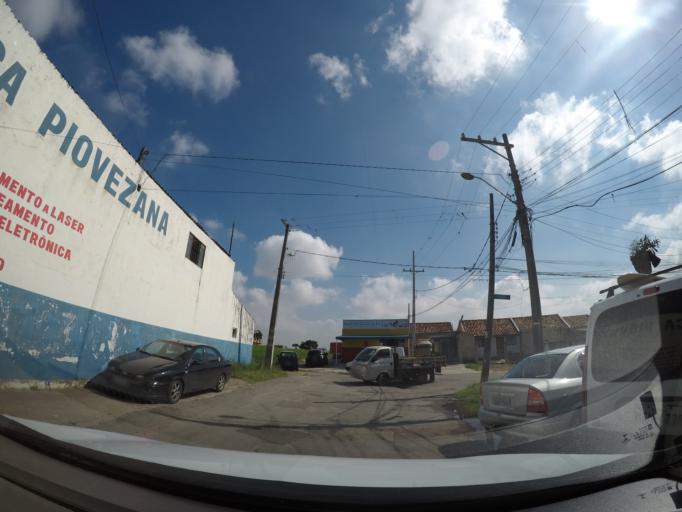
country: BR
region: Parana
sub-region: Sao Jose Dos Pinhais
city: Sao Jose dos Pinhais
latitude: -25.4992
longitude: -49.2216
